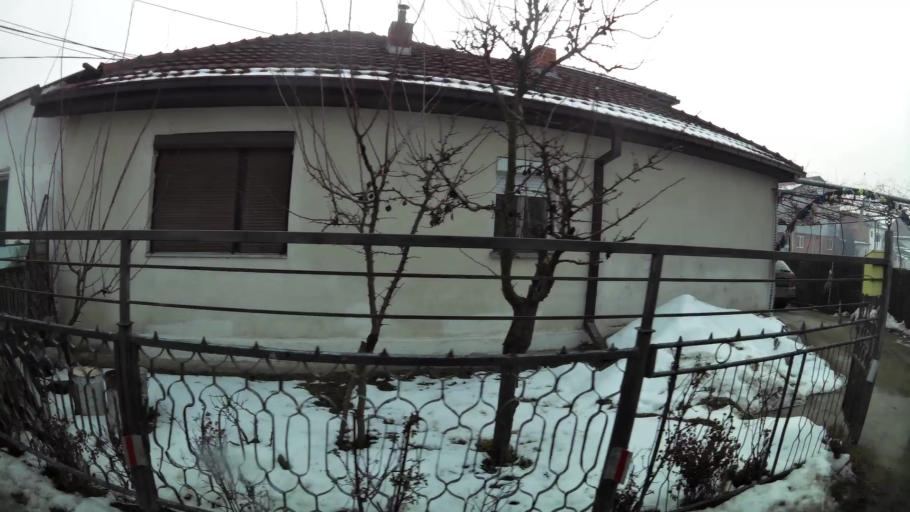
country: MK
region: Ilinden
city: Jurumleri
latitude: 41.9729
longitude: 21.5440
